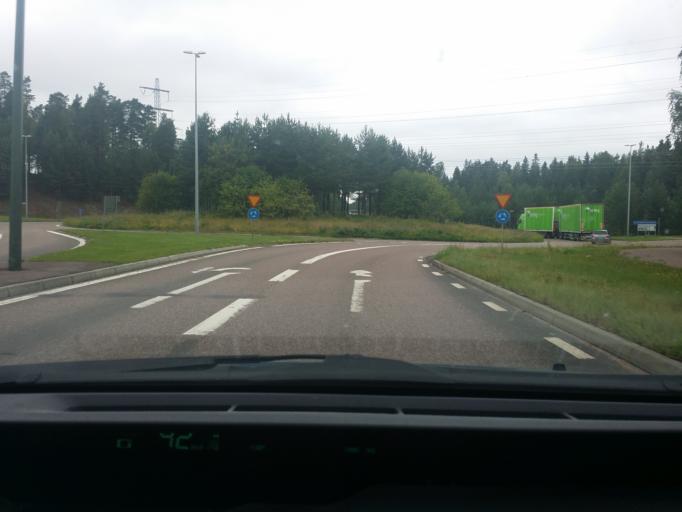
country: SE
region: Dalarna
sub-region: Borlange Kommun
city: Borlaenge
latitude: 60.5054
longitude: 15.3880
